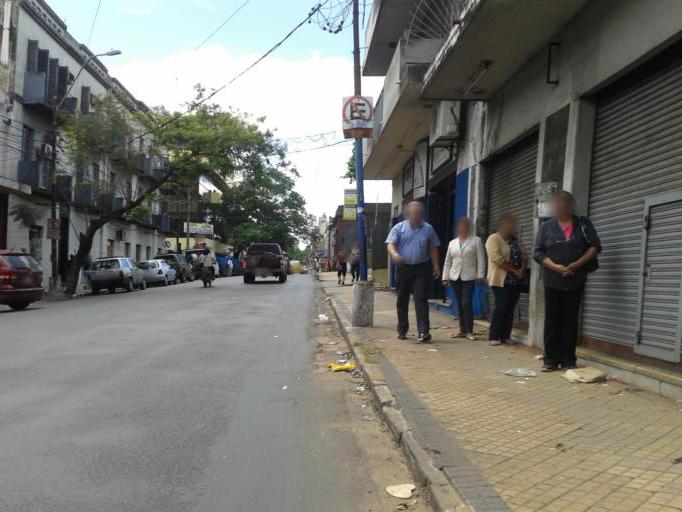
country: PY
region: Asuncion
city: Asuncion
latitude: -25.2871
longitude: -57.6323
